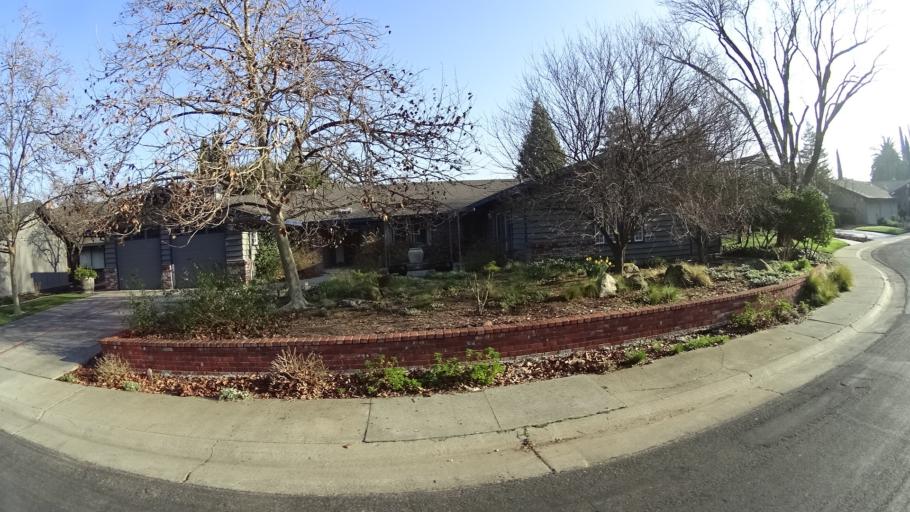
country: US
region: California
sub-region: Yolo County
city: Davis
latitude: 38.5549
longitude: -121.7895
